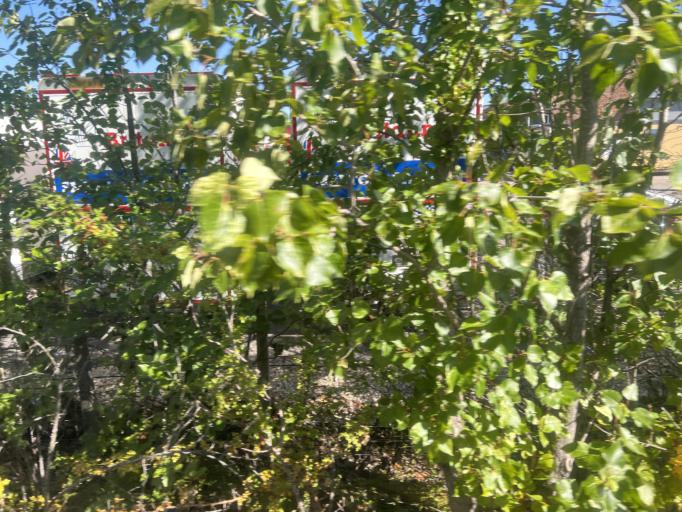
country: GB
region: England
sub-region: Lincolnshire
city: Heckington
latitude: 52.9770
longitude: -0.2922
